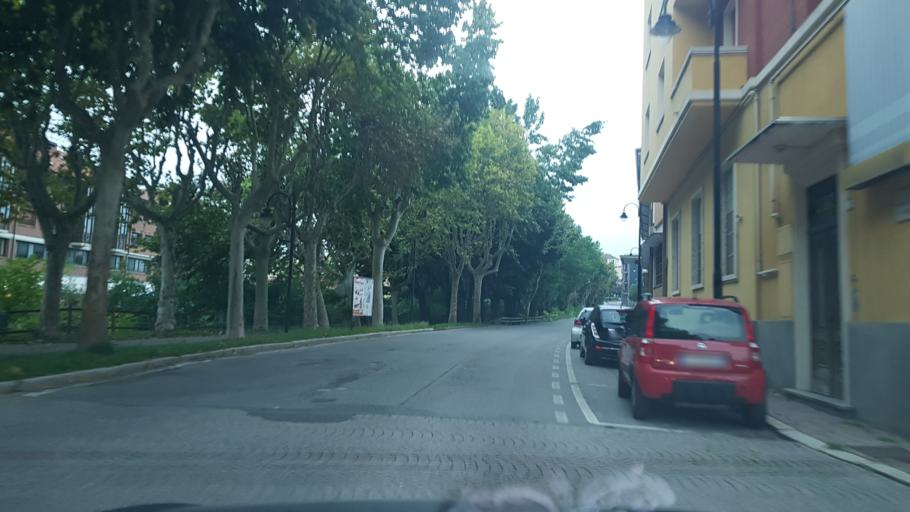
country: IT
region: Piedmont
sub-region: Provincia di Cuneo
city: Mondovi
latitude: 44.3892
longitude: 7.8195
